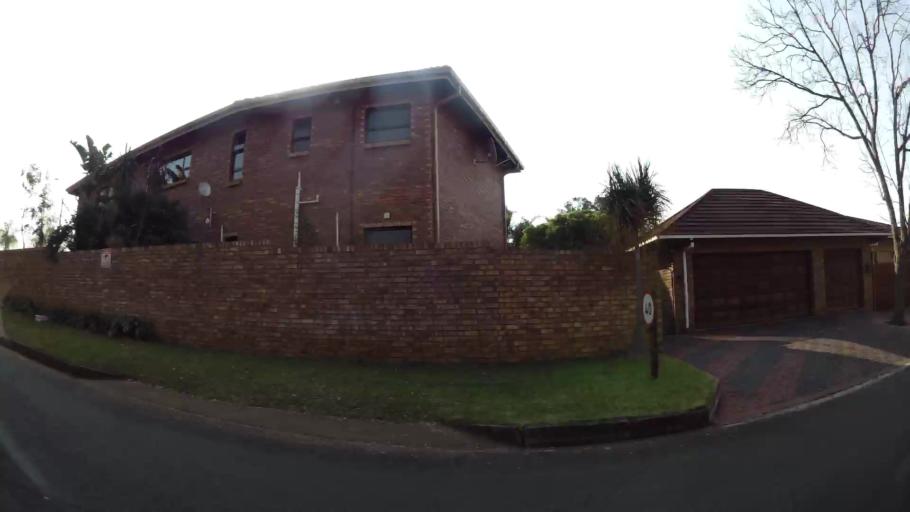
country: ZA
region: Gauteng
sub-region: City of Johannesburg Metropolitan Municipality
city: Modderfontein
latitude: -26.0774
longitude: 28.2047
